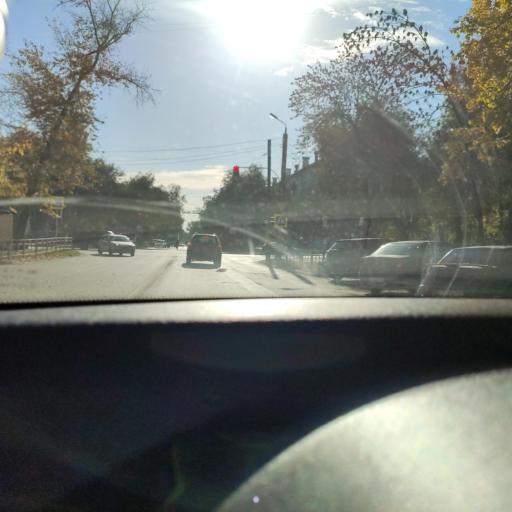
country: RU
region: Samara
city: Samara
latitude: 53.2168
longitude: 50.2359
